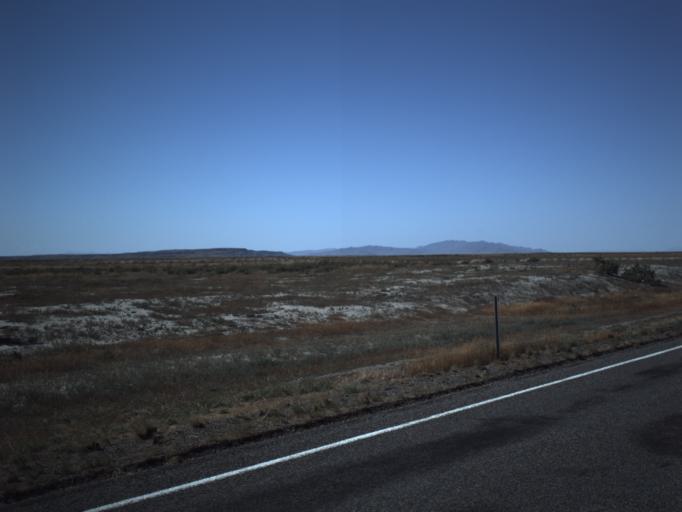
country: US
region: Utah
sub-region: Millard County
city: Delta
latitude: 39.3269
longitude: -112.7282
